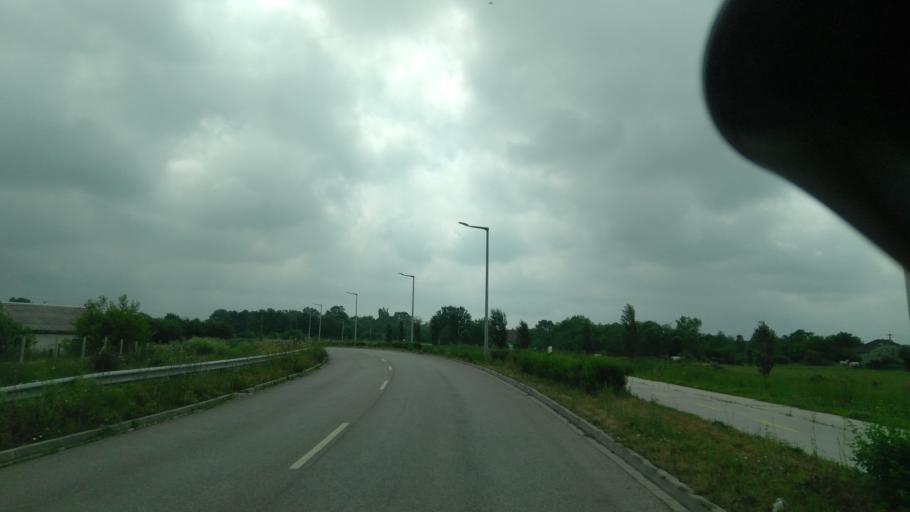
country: HU
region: Bekes
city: Bekescsaba
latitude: 46.6538
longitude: 21.0894
